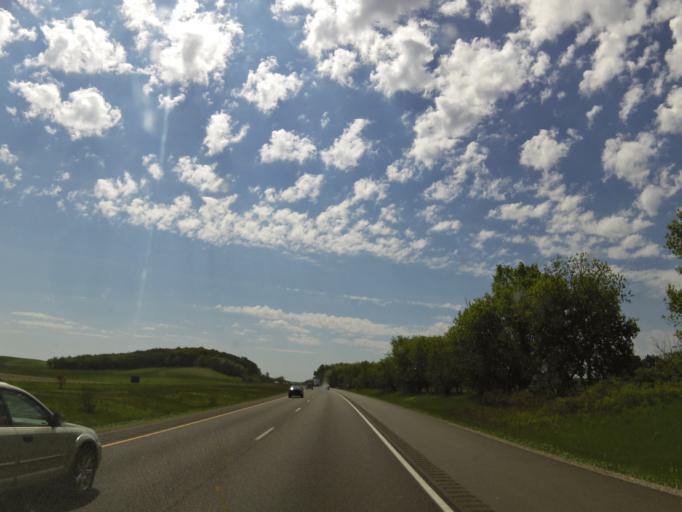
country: US
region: Wisconsin
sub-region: Eau Claire County
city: Fall Creek
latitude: 44.6949
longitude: -91.3391
